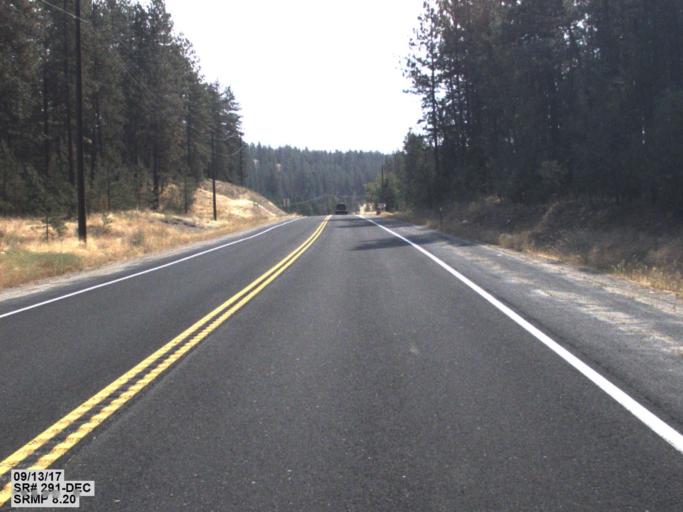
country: US
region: Washington
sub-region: Spokane County
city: Fairwood
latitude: 47.7650
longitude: -117.5448
